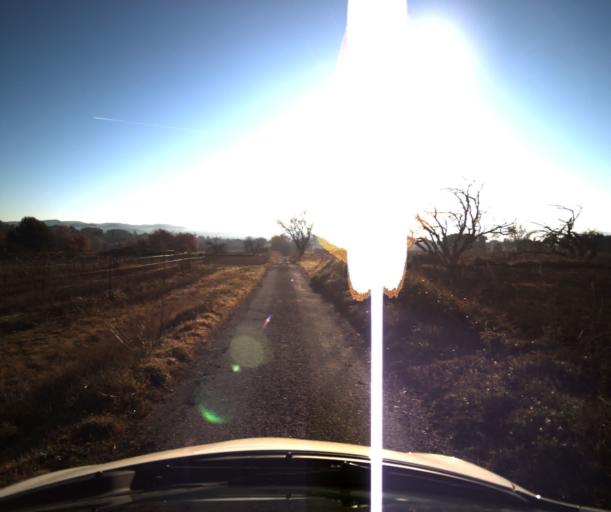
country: FR
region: Provence-Alpes-Cote d'Azur
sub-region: Departement du Vaucluse
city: Pertuis
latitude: 43.7065
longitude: 5.4906
